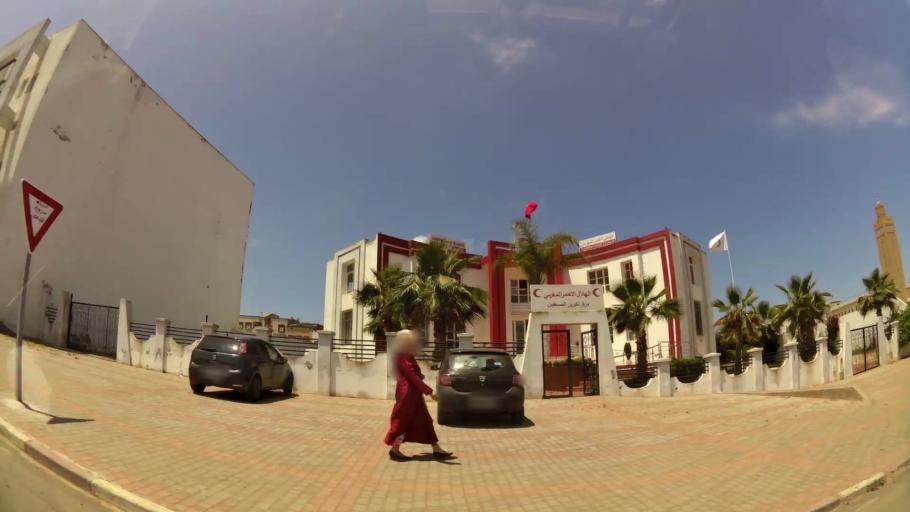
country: MA
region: Gharb-Chrarda-Beni Hssen
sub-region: Kenitra Province
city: Kenitra
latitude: 34.2582
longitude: -6.6116
